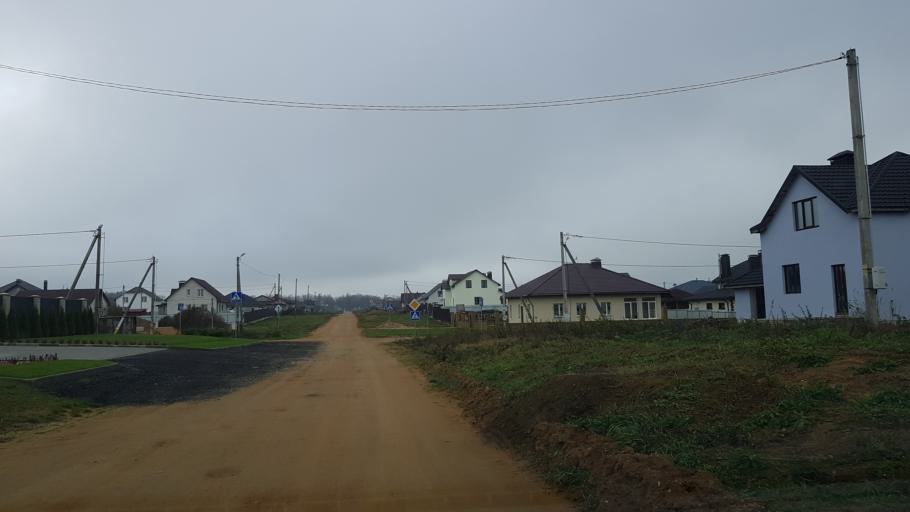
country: BY
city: Fanipol
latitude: 53.7316
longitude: 27.3217
